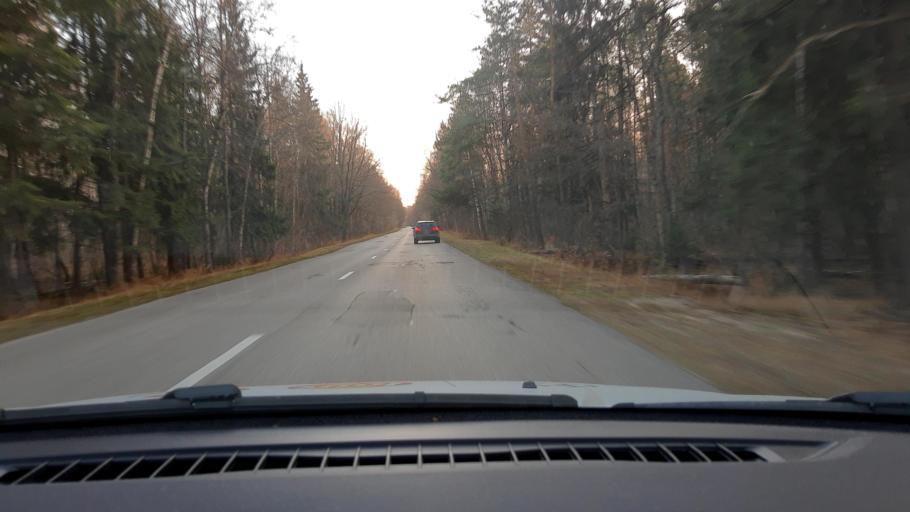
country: RU
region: Nizjnij Novgorod
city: Volodarsk
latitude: 56.2656
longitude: 43.1680
